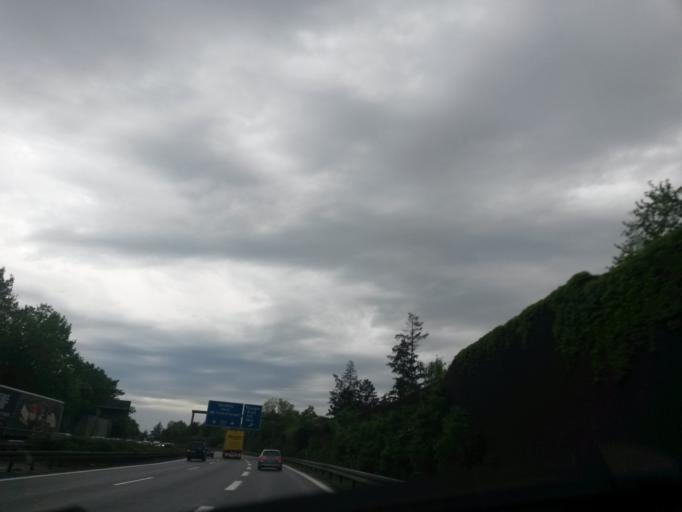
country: DE
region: Bavaria
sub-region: Regierungsbezirk Mittelfranken
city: Erlangen
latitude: 49.5887
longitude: 10.9920
